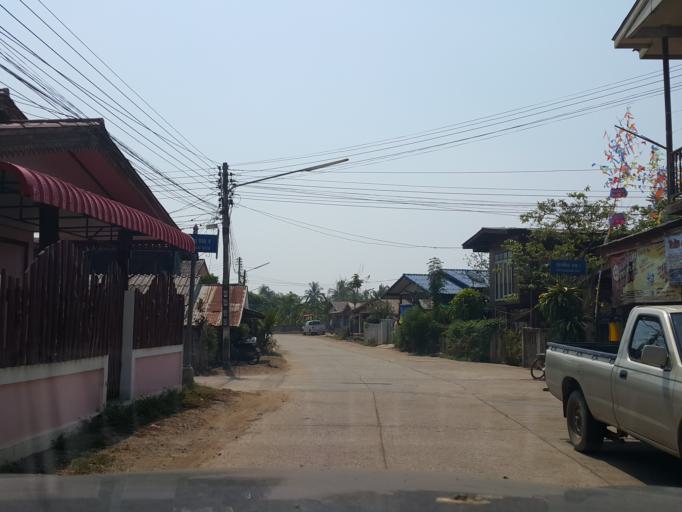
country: TH
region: Sukhothai
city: Thung Saliam
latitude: 17.3119
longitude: 99.5541
